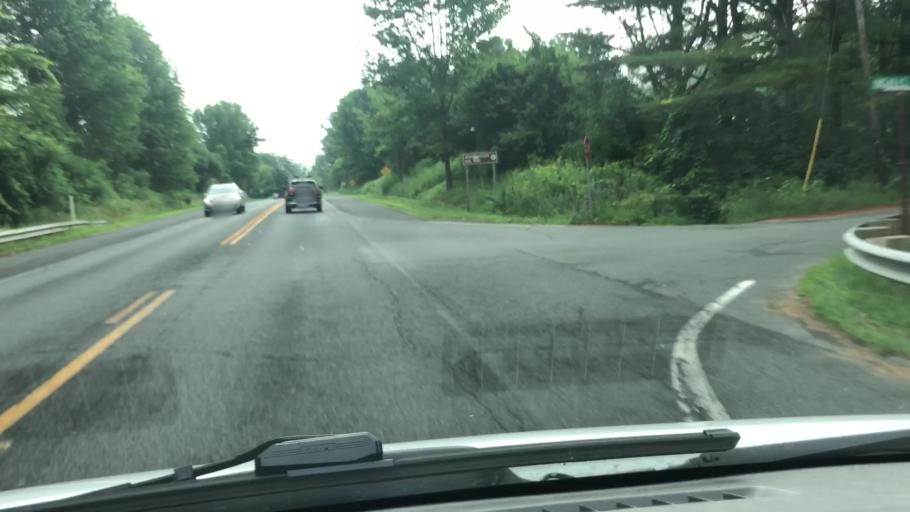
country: US
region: Massachusetts
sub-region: Berkshire County
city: Lanesborough
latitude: 42.5359
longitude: -73.1834
